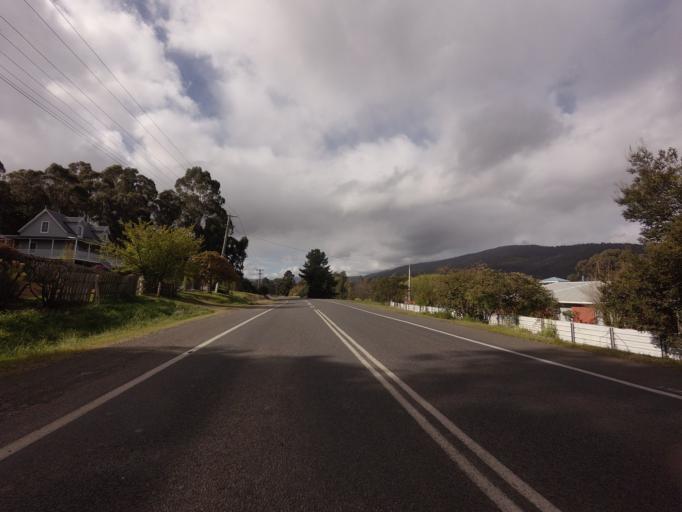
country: AU
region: Tasmania
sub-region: Huon Valley
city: Franklin
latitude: -43.0622
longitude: 147.0269
